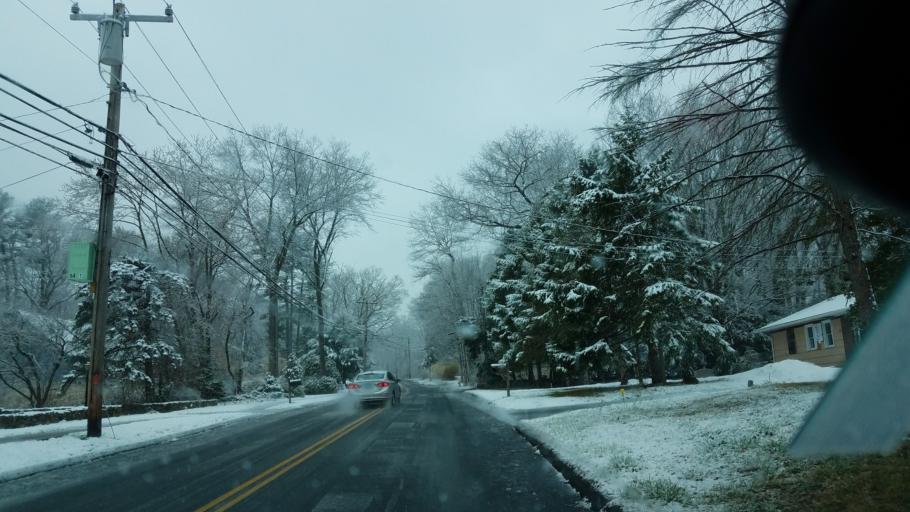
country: US
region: Connecticut
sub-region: New Haven County
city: Cheshire
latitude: 41.4872
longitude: -72.9229
